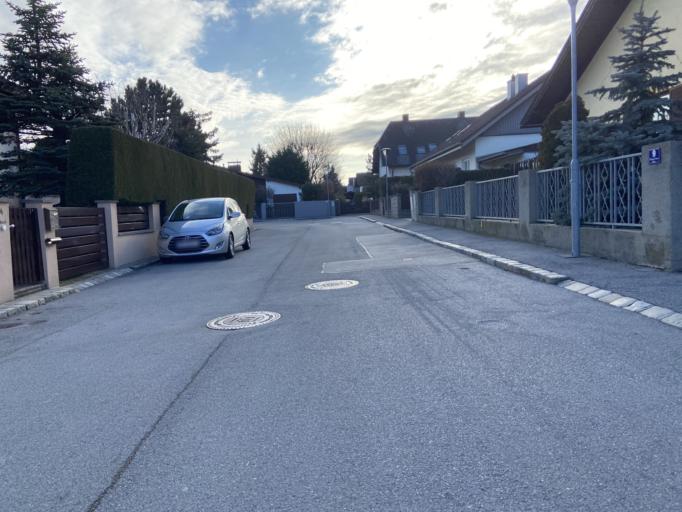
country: AT
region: Lower Austria
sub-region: Politischer Bezirk Modling
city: Neu-Guntramsdorf
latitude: 48.0555
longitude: 16.3174
